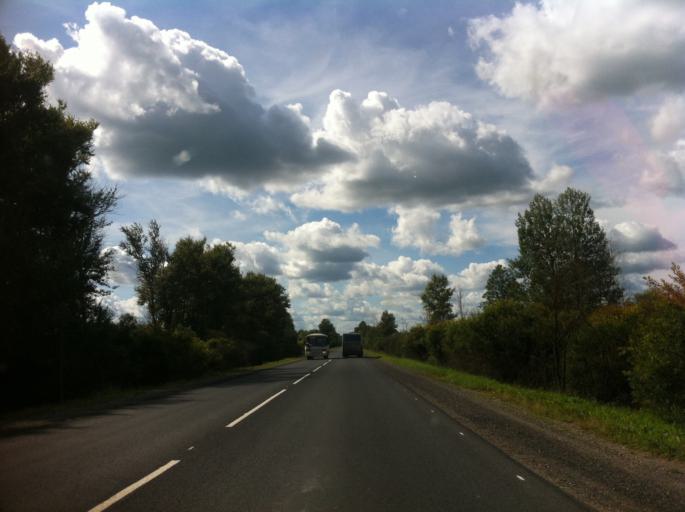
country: RU
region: Pskov
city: Izborsk
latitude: 57.7267
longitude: 27.9579
